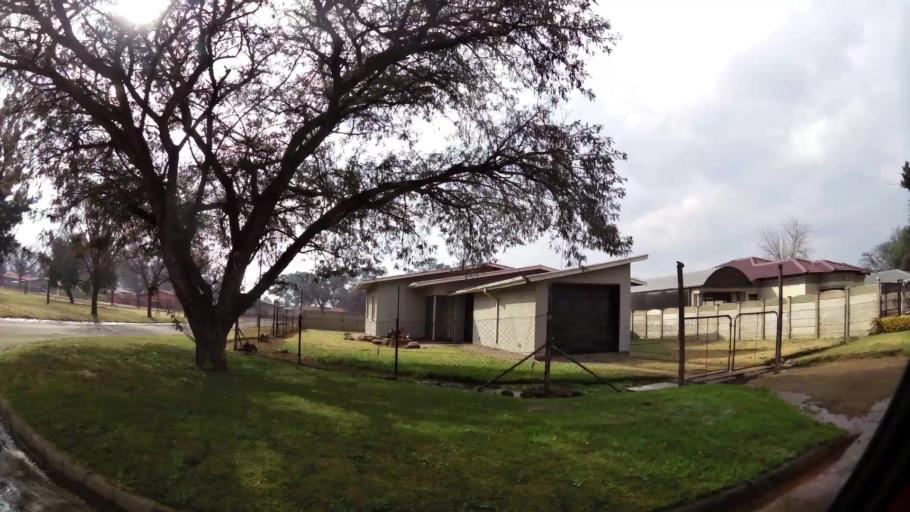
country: ZA
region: Gauteng
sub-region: Sedibeng District Municipality
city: Vanderbijlpark
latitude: -26.6784
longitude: 27.8366
